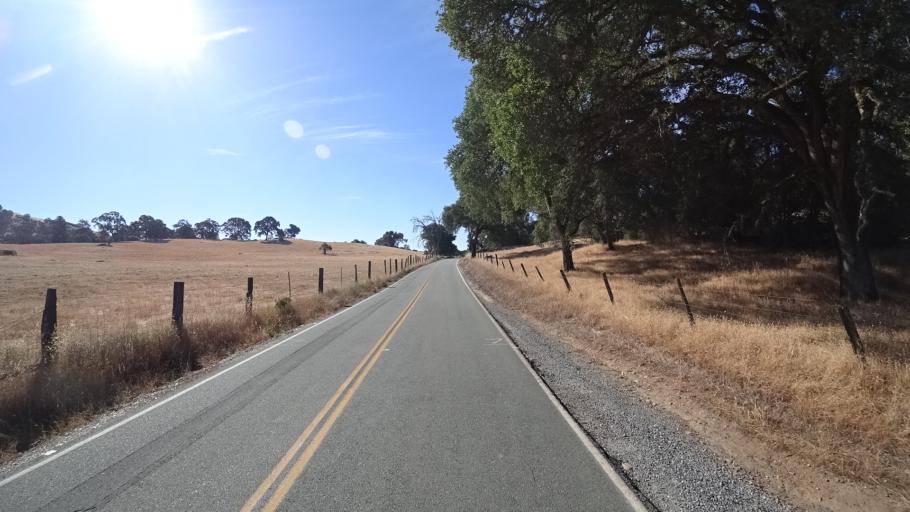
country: US
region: California
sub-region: Calaveras County
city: San Andreas
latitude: 38.1735
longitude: -120.6430
